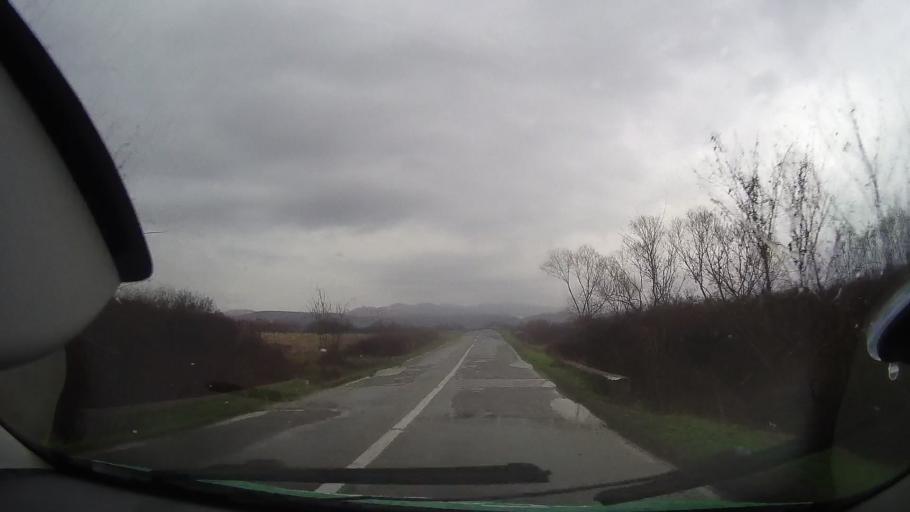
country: RO
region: Bihor
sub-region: Comuna Soimi
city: Soimi
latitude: 46.6987
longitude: 22.0914
